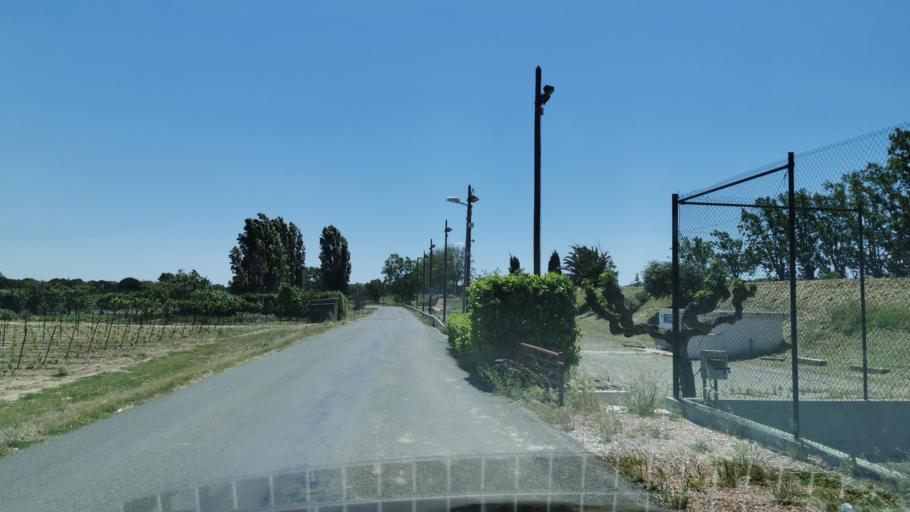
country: FR
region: Languedoc-Roussillon
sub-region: Departement de l'Aude
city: Saint-Marcel-sur-Aude
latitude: 43.2565
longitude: 2.9509
